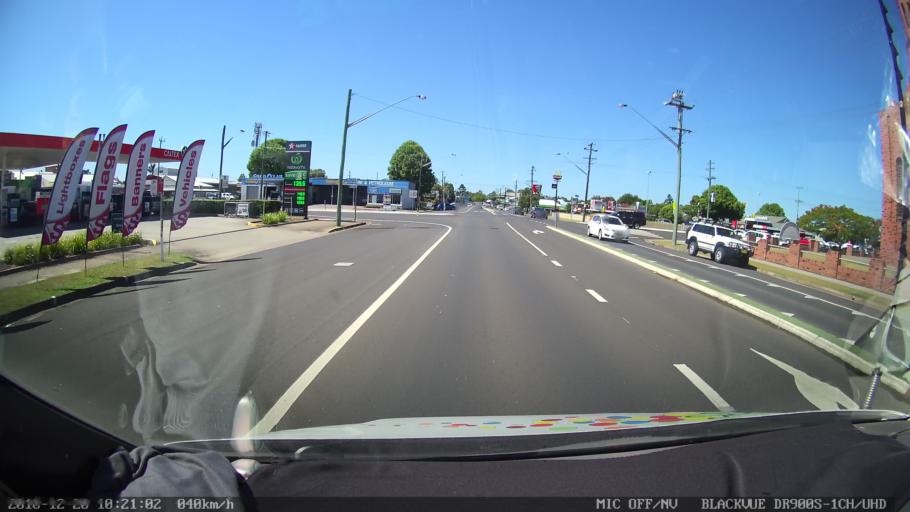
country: AU
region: New South Wales
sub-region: Richmond Valley
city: Casino
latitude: -28.8620
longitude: 153.0462
